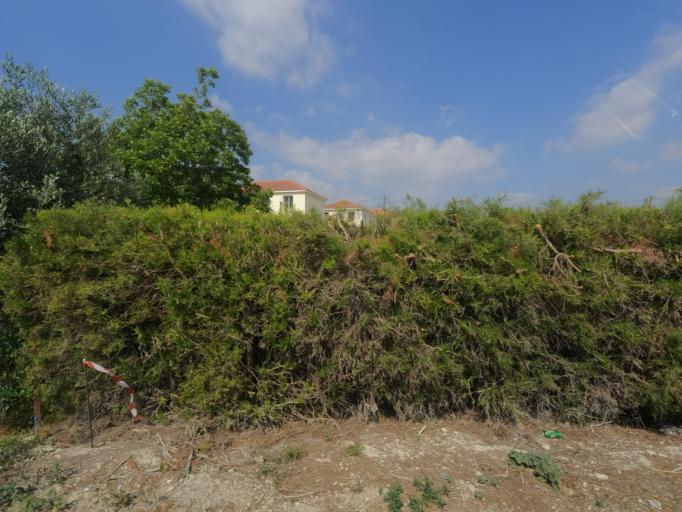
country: CY
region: Larnaka
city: Aradippou
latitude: 34.9245
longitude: 33.5372
